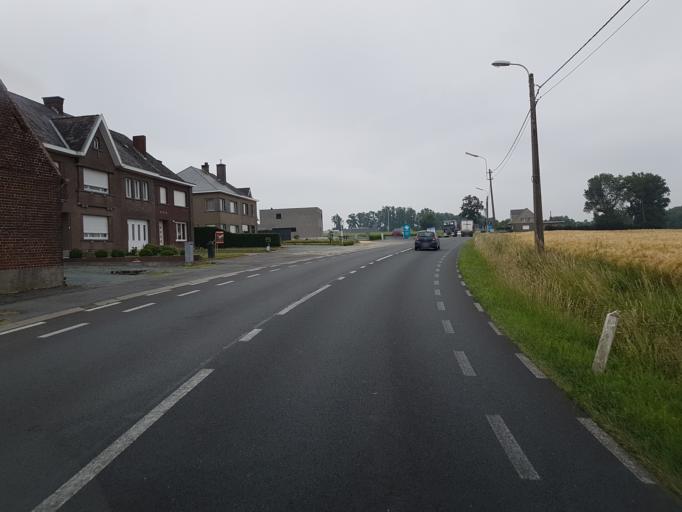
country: BE
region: Flanders
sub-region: Provincie Oost-Vlaanderen
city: Perre
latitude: 50.8566
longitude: 3.8575
